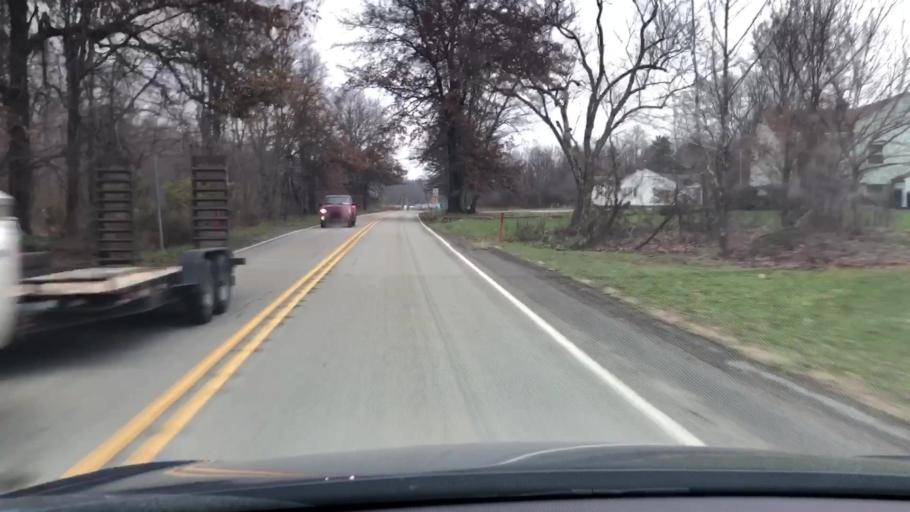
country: US
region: Pennsylvania
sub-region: Westmoreland County
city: New Stanton
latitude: 40.2032
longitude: -79.6241
